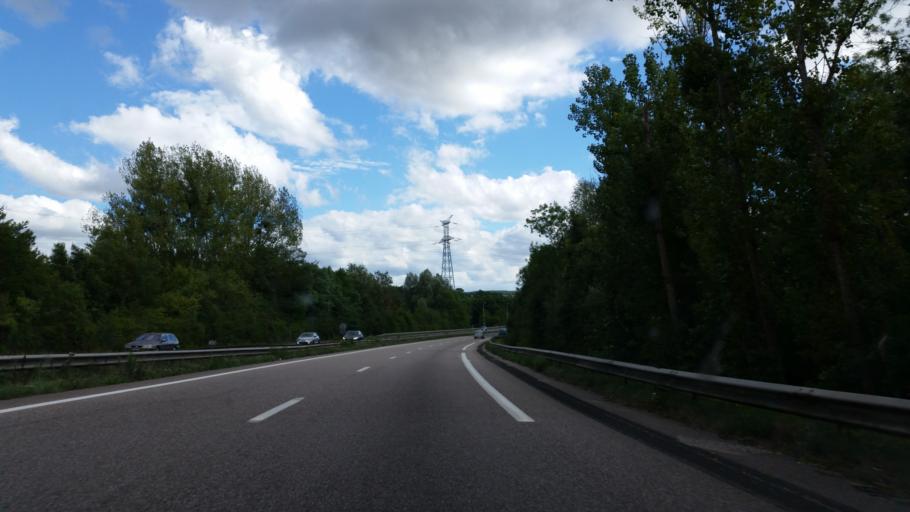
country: FR
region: Lorraine
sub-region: Departement de Meurthe-et-Moselle
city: Richardmenil
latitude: 48.5875
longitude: 6.1759
